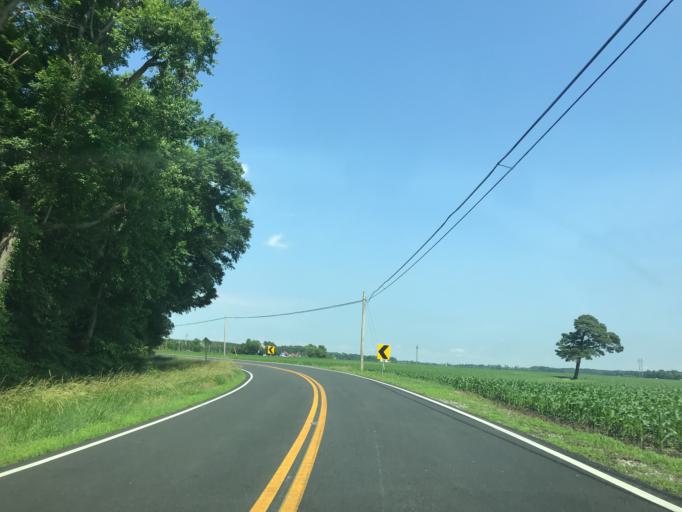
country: US
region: Maryland
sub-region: Dorchester County
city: Hurlock
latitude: 38.5744
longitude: -75.8307
